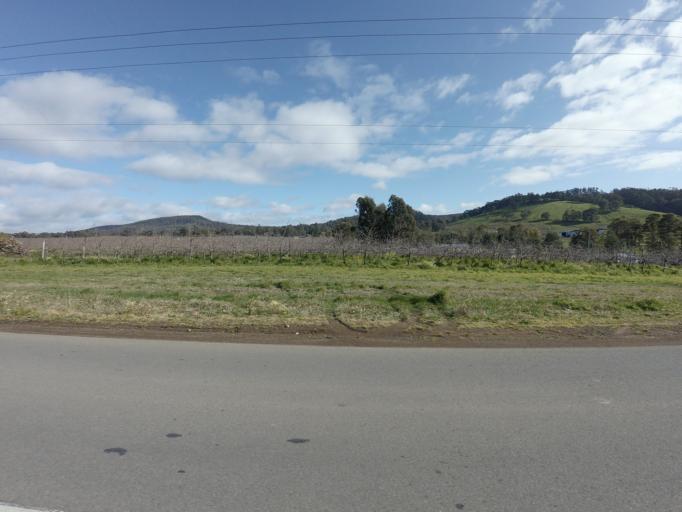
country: AU
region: Tasmania
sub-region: Huon Valley
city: Geeveston
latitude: -43.3230
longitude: 146.9994
